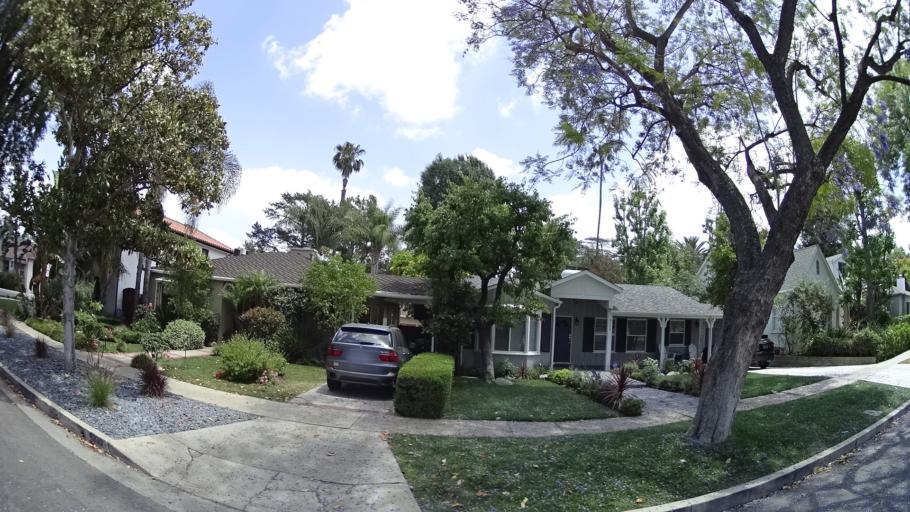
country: US
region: California
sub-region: Los Angeles County
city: Sherman Oaks
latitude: 34.1467
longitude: -118.4351
